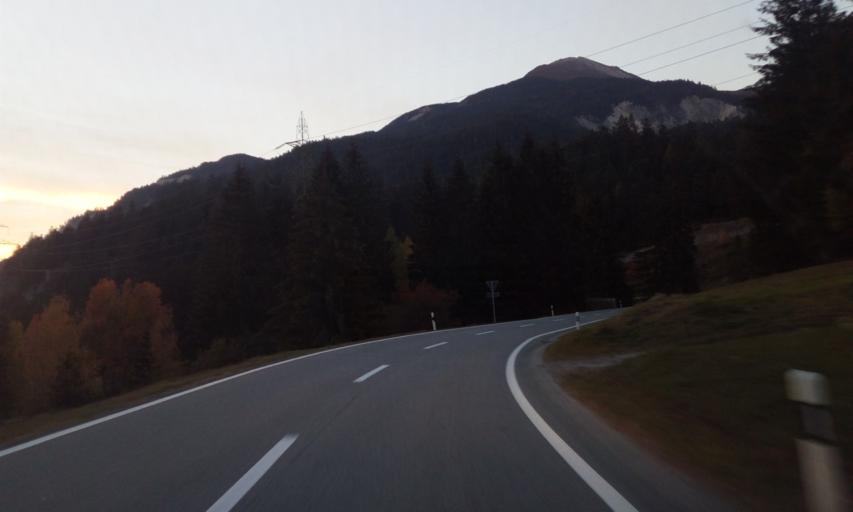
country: CH
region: Grisons
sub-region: Albula District
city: Tiefencastel
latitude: 46.6673
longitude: 9.6274
